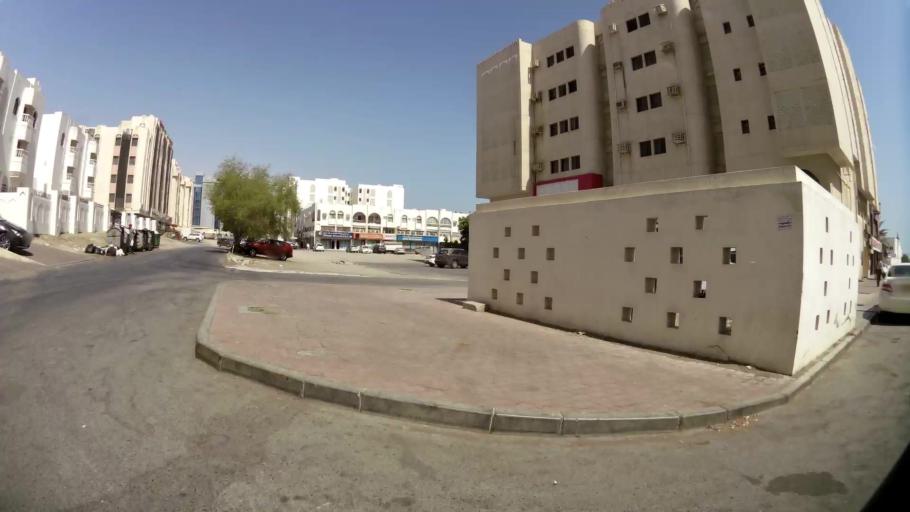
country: OM
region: Muhafazat Masqat
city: Bawshar
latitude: 23.5961
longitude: 58.4210
